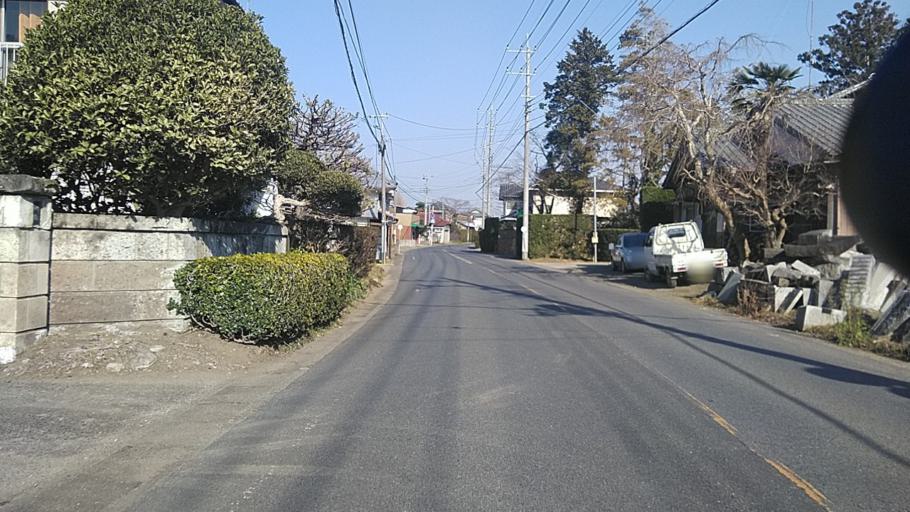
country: JP
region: Chiba
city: Yokaichiba
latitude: 35.6946
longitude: 140.5337
